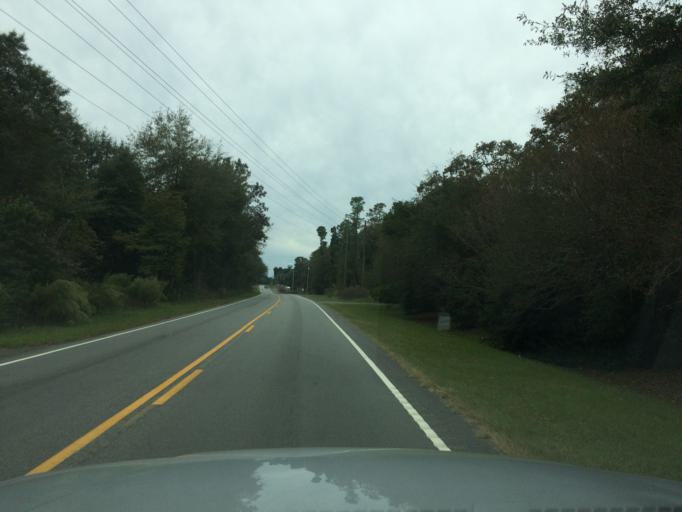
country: US
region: South Carolina
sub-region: Aiken County
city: New Ellenton
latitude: 33.3954
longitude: -81.7048
